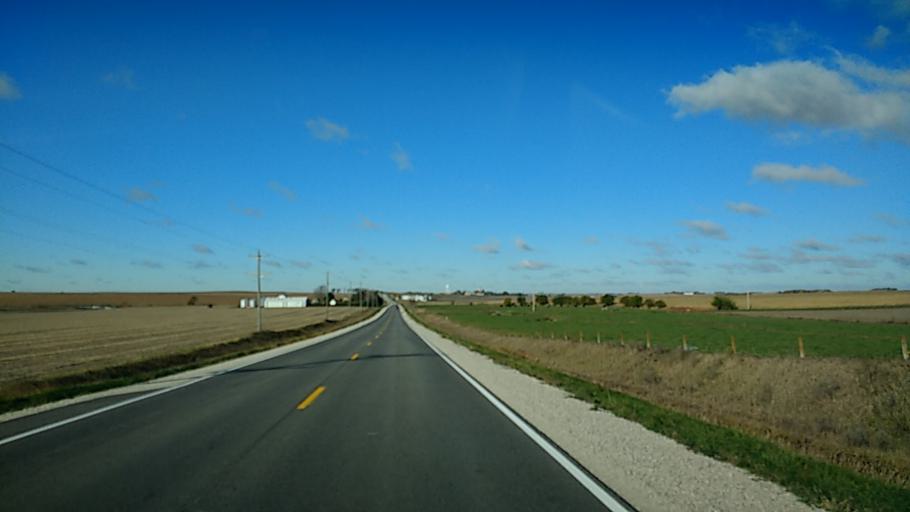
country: US
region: Iowa
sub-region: Ida County
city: Holstein
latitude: 42.5039
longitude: -95.3776
